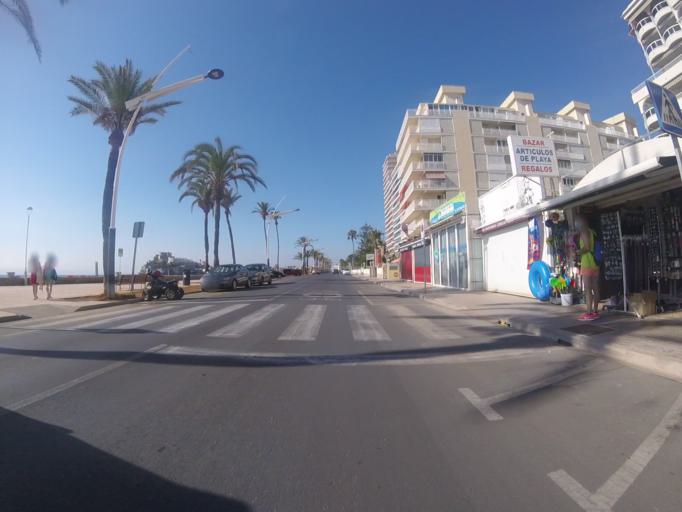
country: ES
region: Valencia
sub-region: Provincia de Castello
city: Peniscola
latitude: 40.3670
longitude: 0.4036
